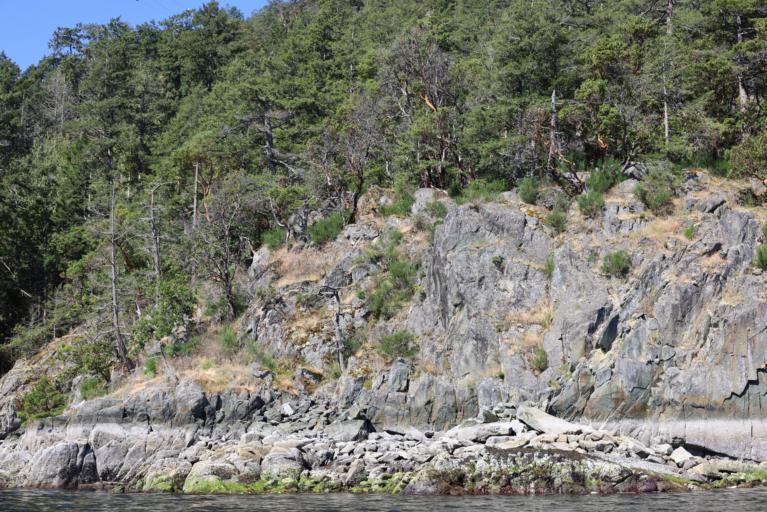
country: CA
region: British Columbia
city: North Cowichan
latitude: 48.8297
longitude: -123.5851
